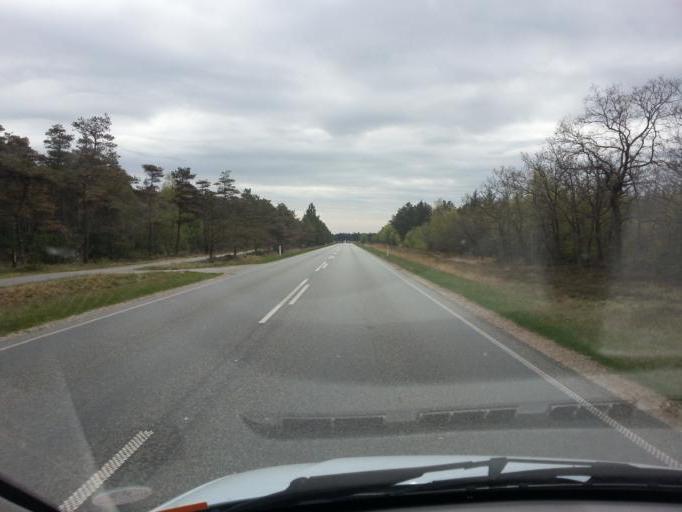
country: DK
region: South Denmark
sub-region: Varde Kommune
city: Oksbol
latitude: 55.5992
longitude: 8.2249
